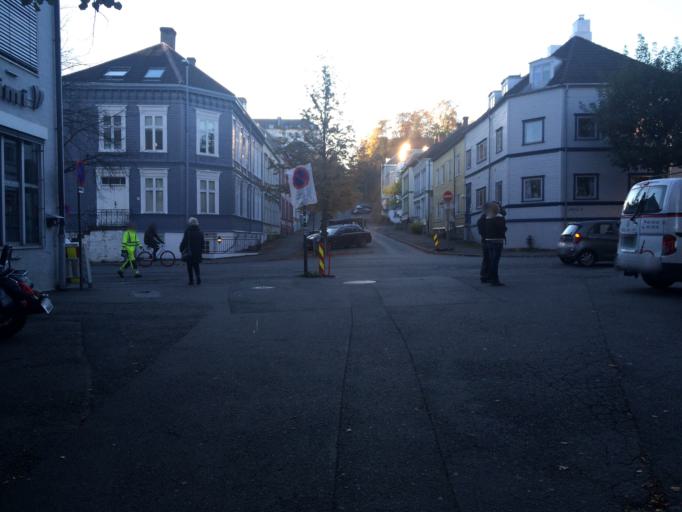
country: NO
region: Sor-Trondelag
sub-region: Trondheim
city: Trondheim
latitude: 63.4335
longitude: 10.4133
